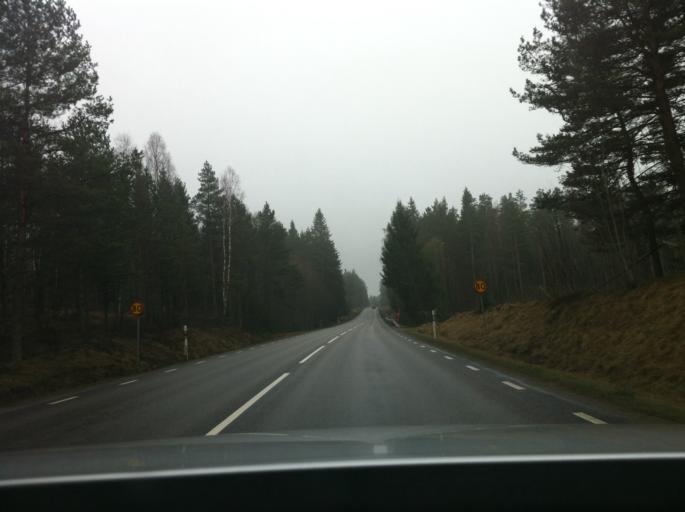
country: SE
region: Vaestra Goetaland
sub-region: Svenljunga Kommun
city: Svenljunga
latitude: 57.5619
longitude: 13.1253
